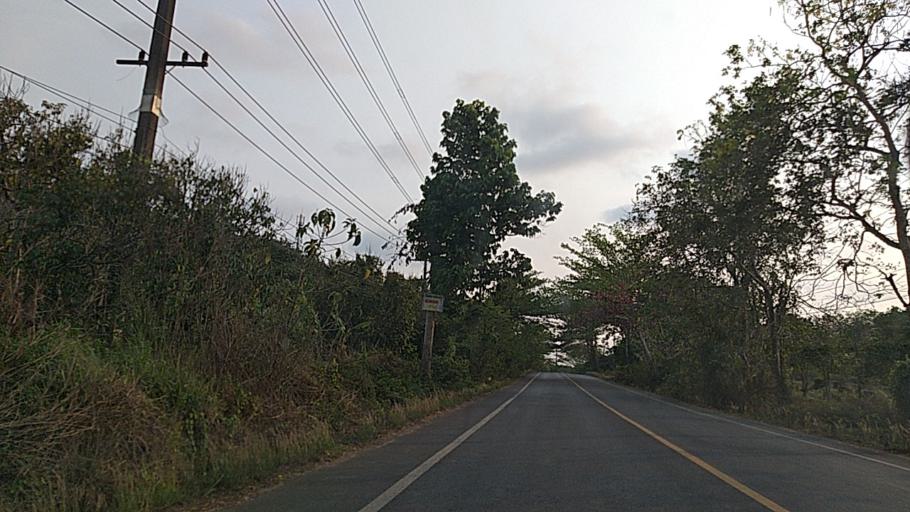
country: TH
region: Trat
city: Khao Saming
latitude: 12.3279
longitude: 102.3692
